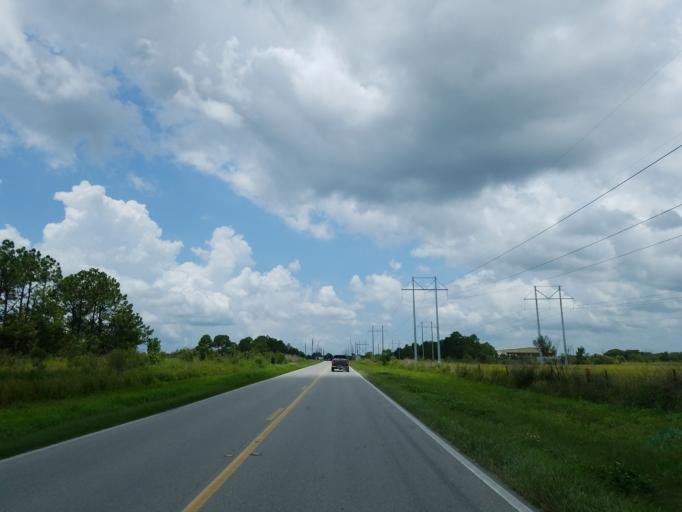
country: US
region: Florida
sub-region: Polk County
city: Willow Oak
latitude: 27.8507
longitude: -82.0480
